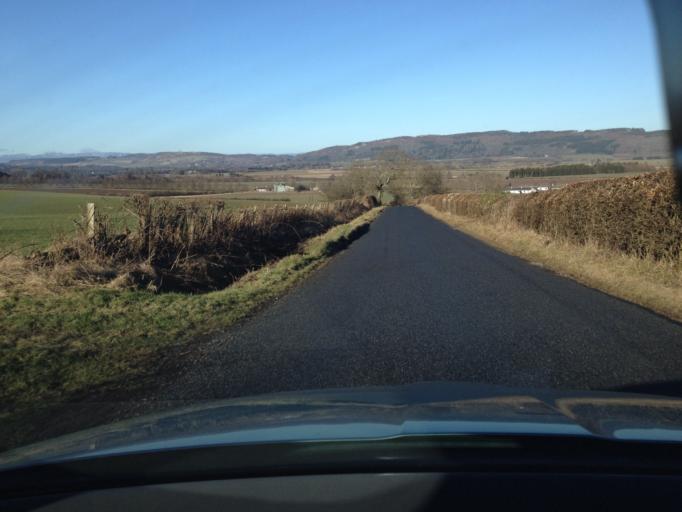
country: GB
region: Scotland
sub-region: Perth and Kinross
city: Bridge of Earn
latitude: 56.3203
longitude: -3.3718
